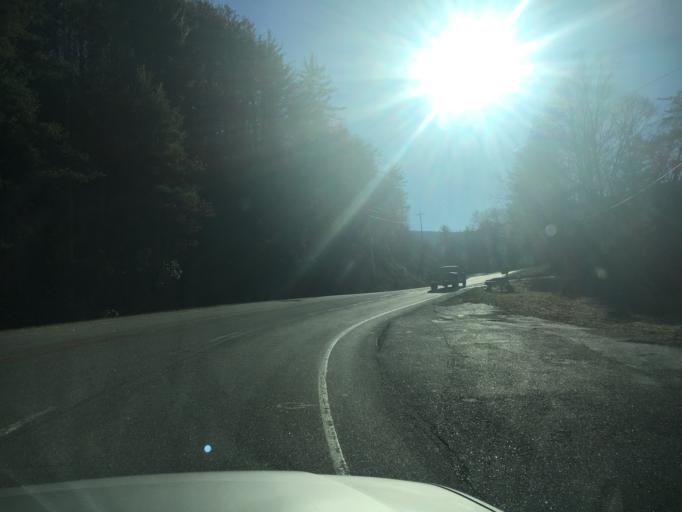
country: US
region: Georgia
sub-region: Union County
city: Blairsville
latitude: 34.7725
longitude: -83.9138
